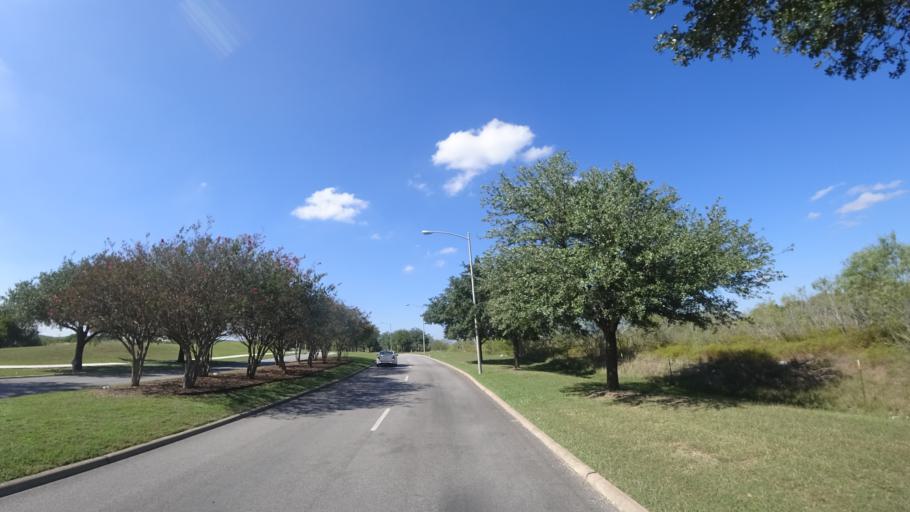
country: US
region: Texas
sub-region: Travis County
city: Manor
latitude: 30.3377
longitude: -97.6086
